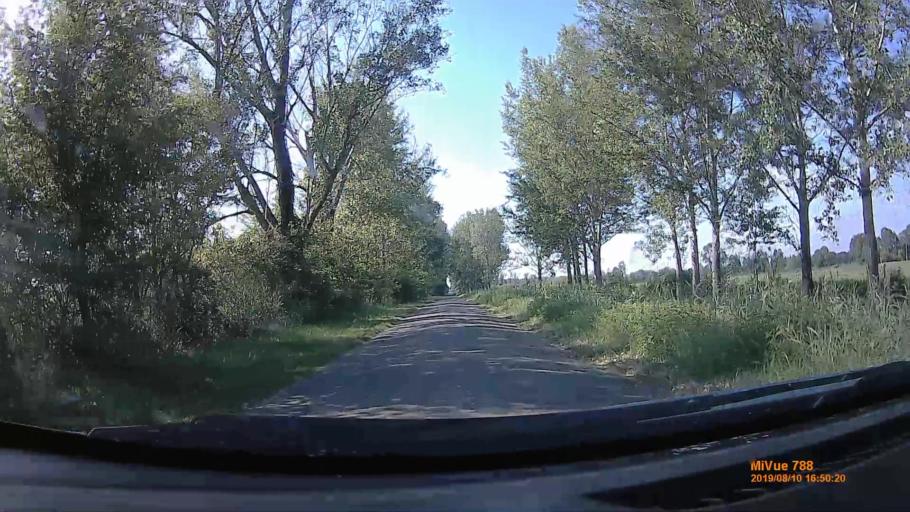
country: HU
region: Somogy
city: Balatonfenyves
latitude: 46.6925
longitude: 17.4916
